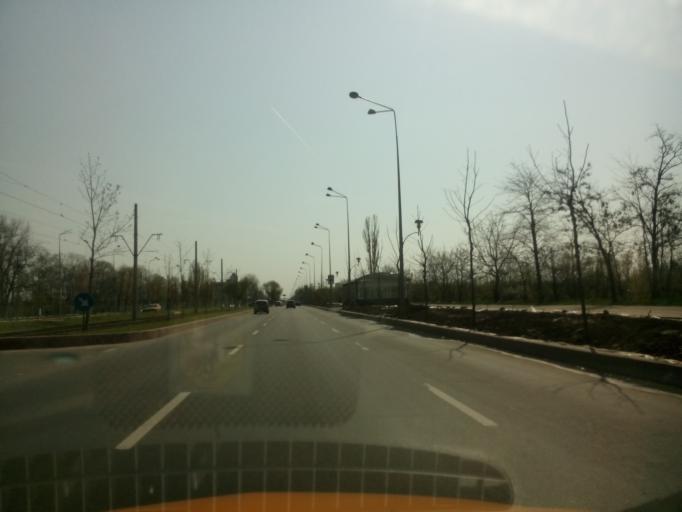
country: RO
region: Ilfov
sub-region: Comuna Glina
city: Catelu
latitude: 44.4074
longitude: 26.1947
